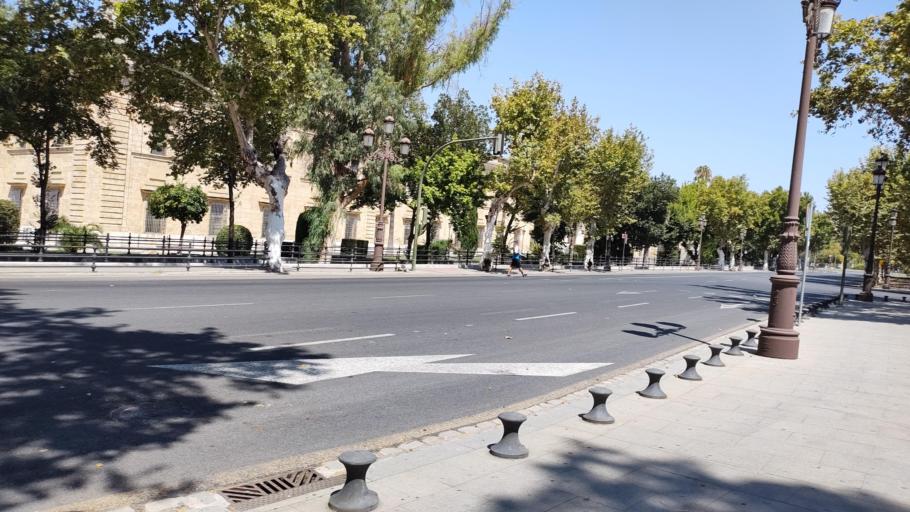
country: ES
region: Andalusia
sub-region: Provincia de Sevilla
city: Sevilla
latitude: 37.3800
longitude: -5.9925
